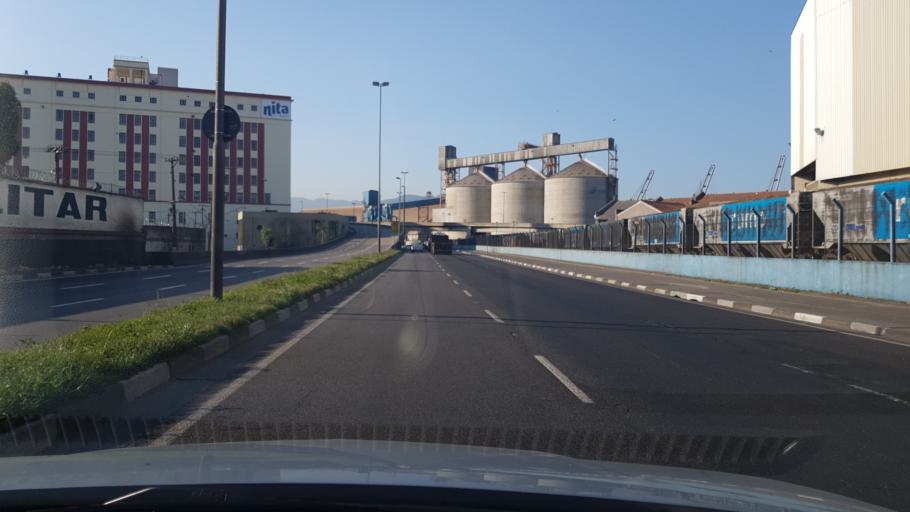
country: BR
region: Sao Paulo
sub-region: Santos
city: Santos
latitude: -23.9400
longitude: -46.3164
